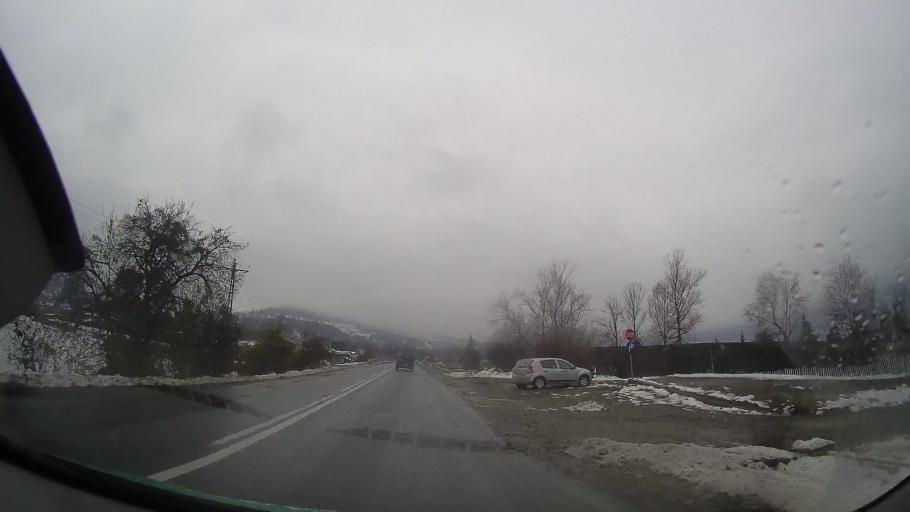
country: RO
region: Neamt
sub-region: Comuna Pangarati
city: Stejaru
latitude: 46.9211
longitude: 26.1893
